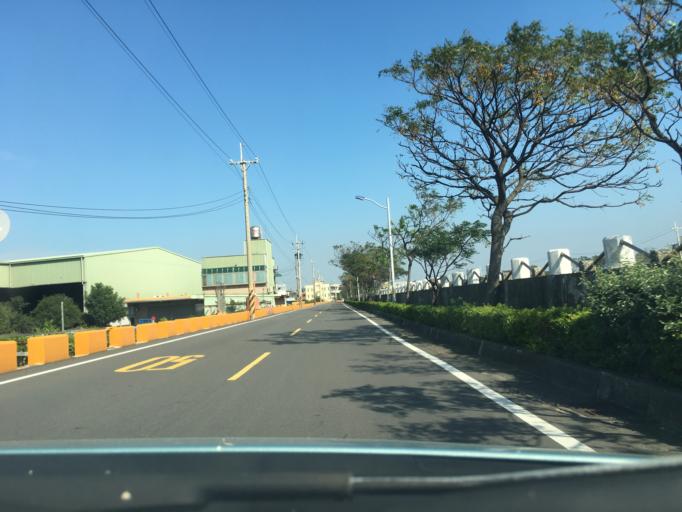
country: TW
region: Taiwan
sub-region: Hsinchu
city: Hsinchu
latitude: 24.8042
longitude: 120.9286
